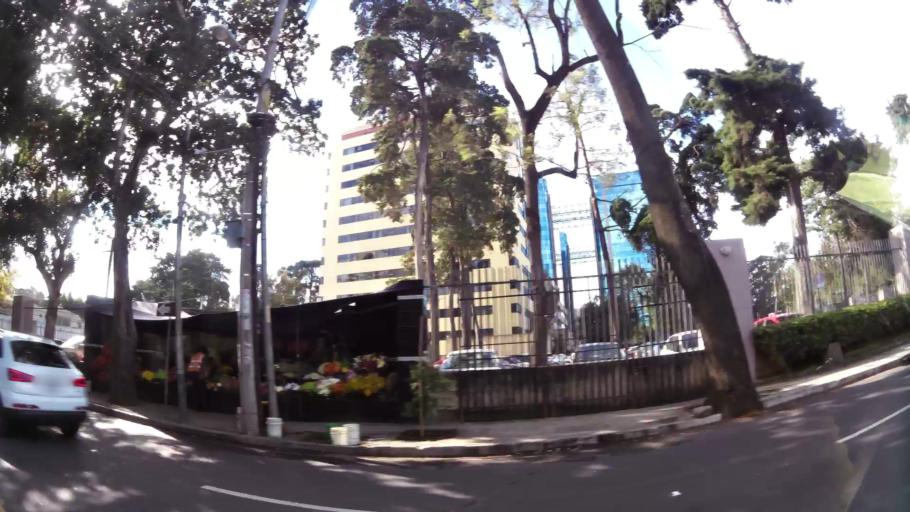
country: GT
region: Guatemala
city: Santa Catarina Pinula
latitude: 14.5887
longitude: -90.5128
